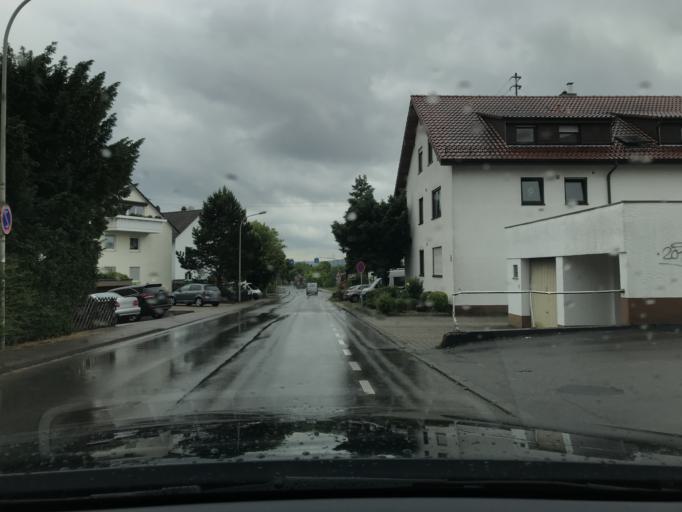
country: DE
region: Baden-Wuerttemberg
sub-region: Regierungsbezirk Stuttgart
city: Korb
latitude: 48.8403
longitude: 9.3537
